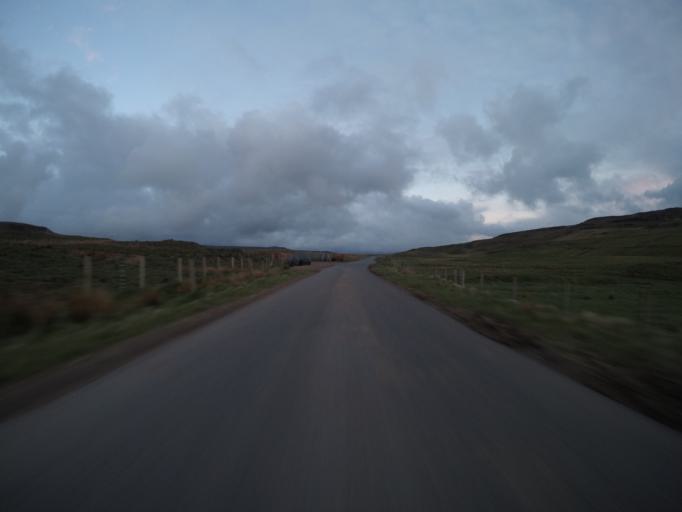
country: GB
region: Scotland
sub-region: Highland
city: Portree
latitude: 57.5993
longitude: -6.3760
